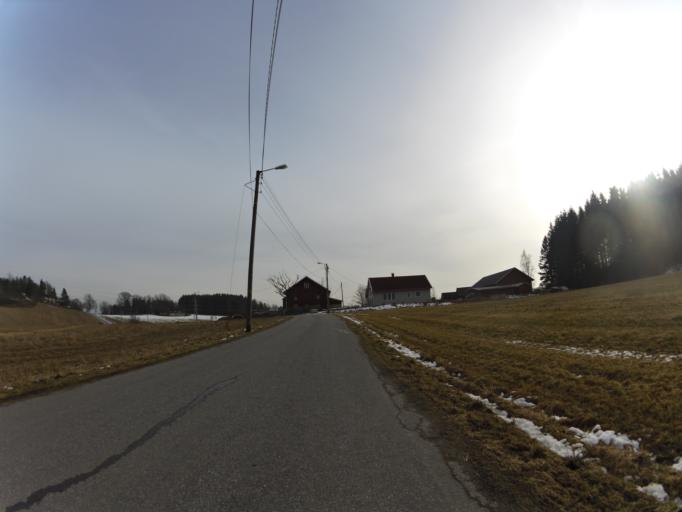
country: NO
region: Ostfold
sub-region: Fredrikstad
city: Fredrikstad
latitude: 59.2749
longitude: 11.0041
